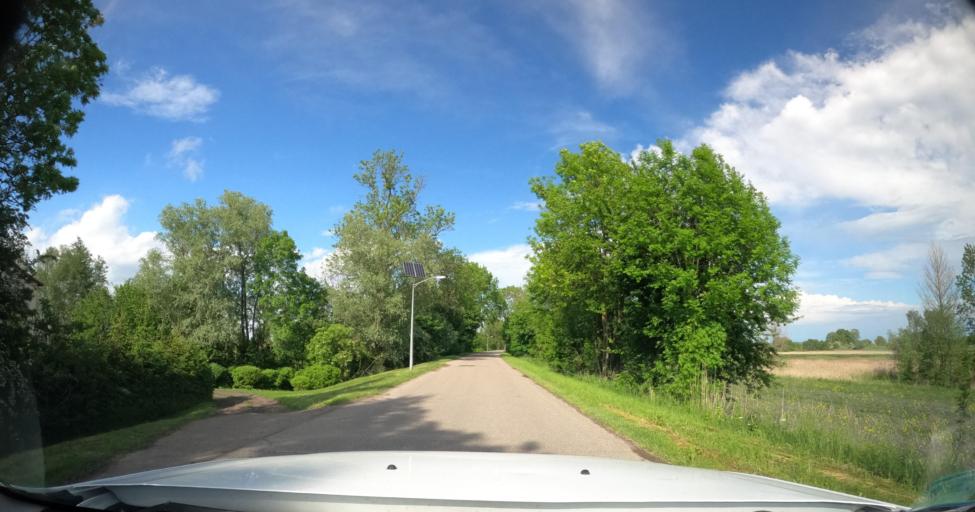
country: PL
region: Warmian-Masurian Voivodeship
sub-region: Powiat elblaski
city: Gronowo Elblaskie
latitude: 54.1764
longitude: 19.2575
